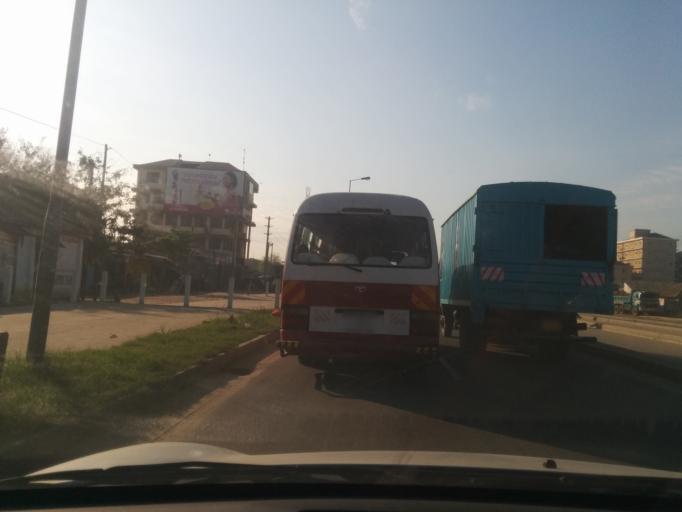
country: TZ
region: Dar es Salaam
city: Magomeni
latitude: -6.8034
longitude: 39.2470
